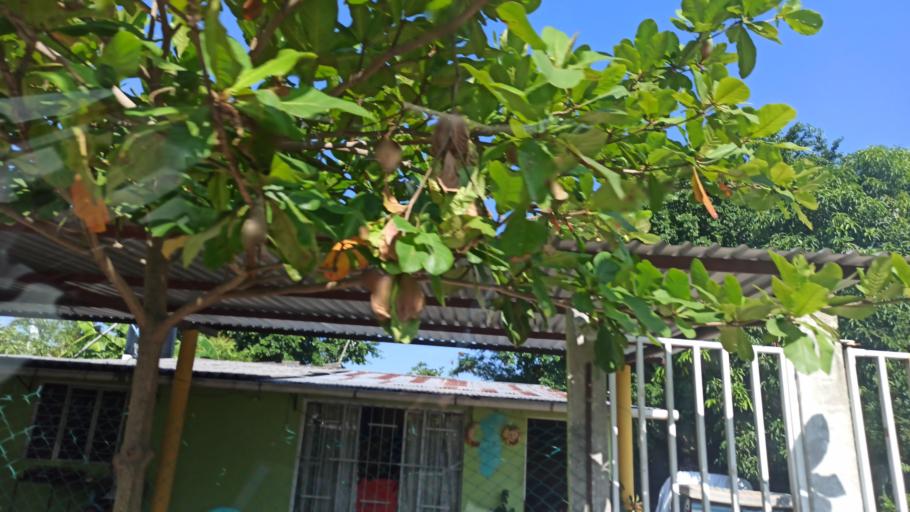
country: MX
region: Veracruz
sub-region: Martinez de la Torre
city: La Union Paso Largo
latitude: 20.1433
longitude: -96.9974
